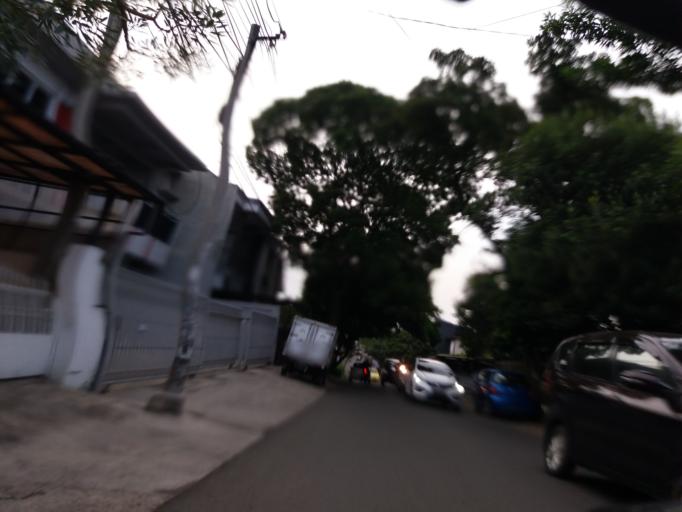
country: ID
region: West Java
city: Bandung
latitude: -6.9385
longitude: 107.6347
